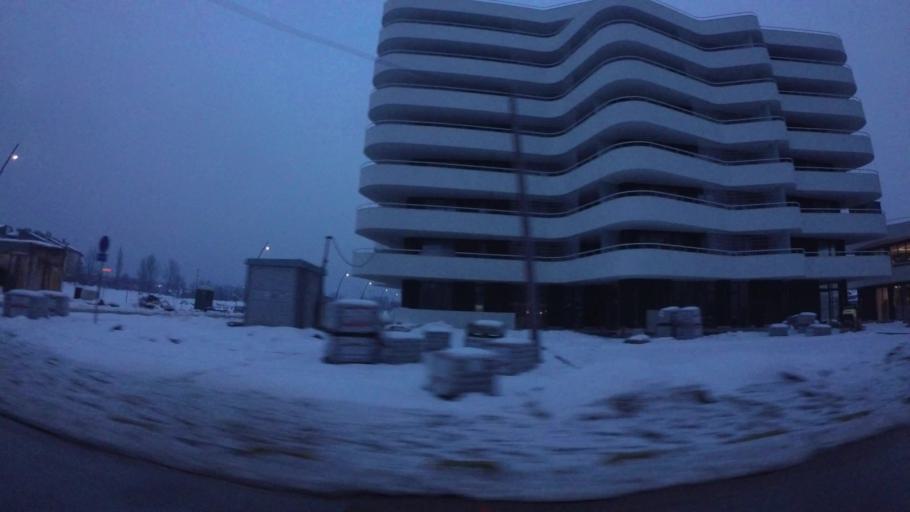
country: BA
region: Federation of Bosnia and Herzegovina
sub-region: Kanton Sarajevo
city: Sarajevo
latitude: 43.8385
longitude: 18.2980
